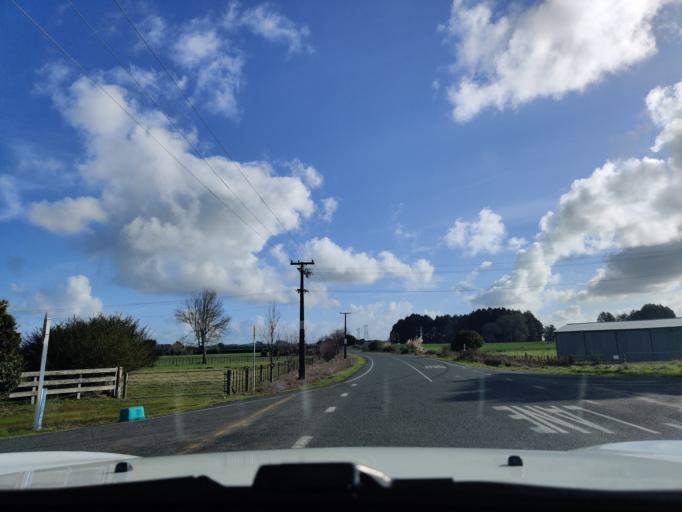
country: NZ
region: Waikato
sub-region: Waikato District
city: Te Kauwhata
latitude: -37.3593
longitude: 175.2613
